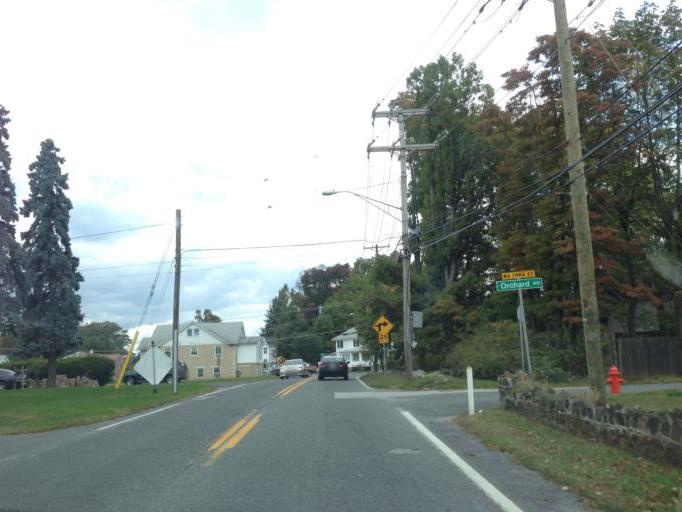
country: US
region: Maryland
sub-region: Baltimore County
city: Milford Mill
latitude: 39.3526
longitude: -76.7673
